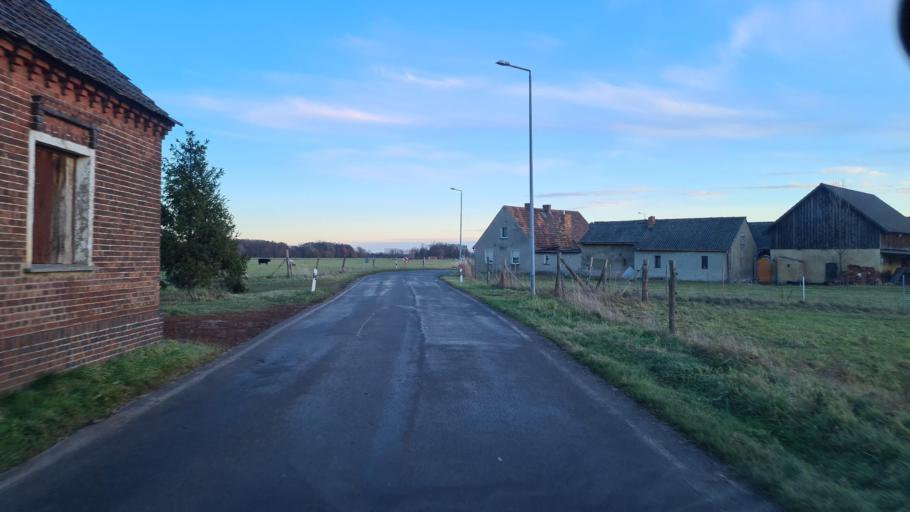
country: DE
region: Brandenburg
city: Burg
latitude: 51.7971
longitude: 14.1437
